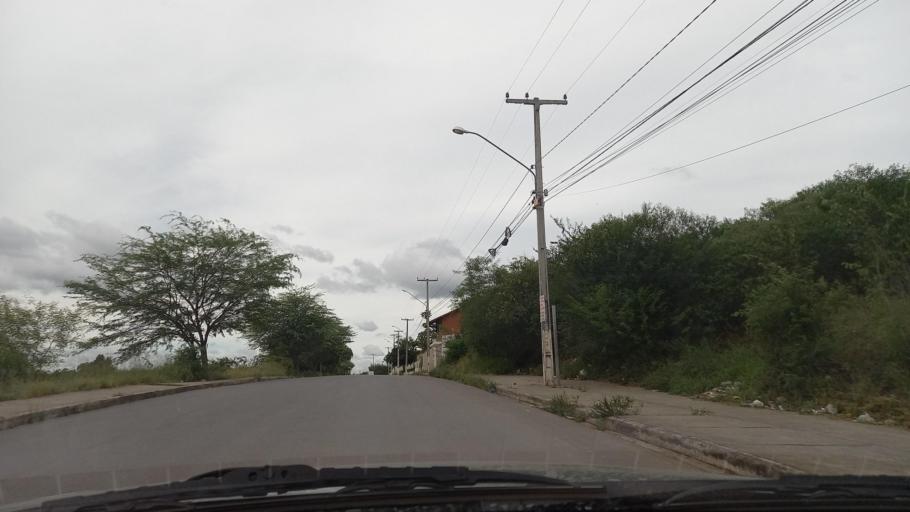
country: BR
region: Pernambuco
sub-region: Gravata
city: Gravata
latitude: -8.2125
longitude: -35.6012
